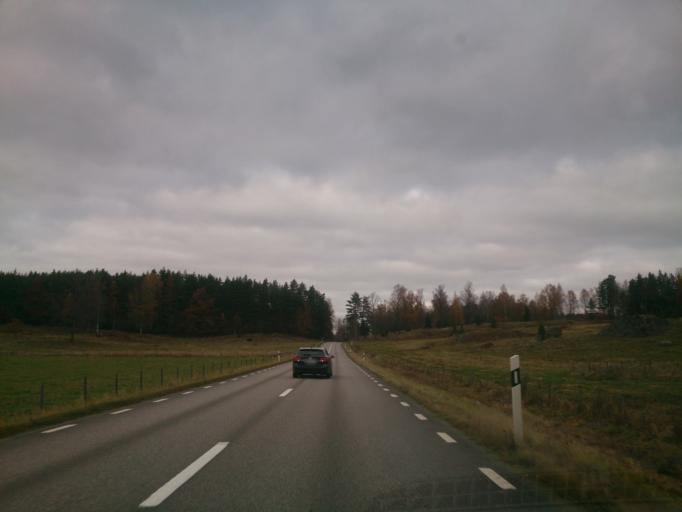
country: SE
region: OEstergoetland
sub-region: Atvidabergs Kommun
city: Atvidaberg
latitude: 58.2977
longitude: 15.8906
